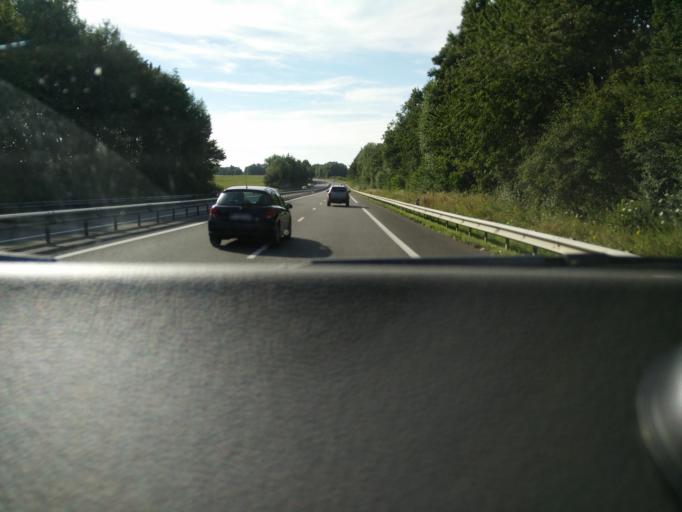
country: FR
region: Nord-Pas-de-Calais
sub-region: Departement du Nord
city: Bavay
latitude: 50.3013
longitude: 3.8065
